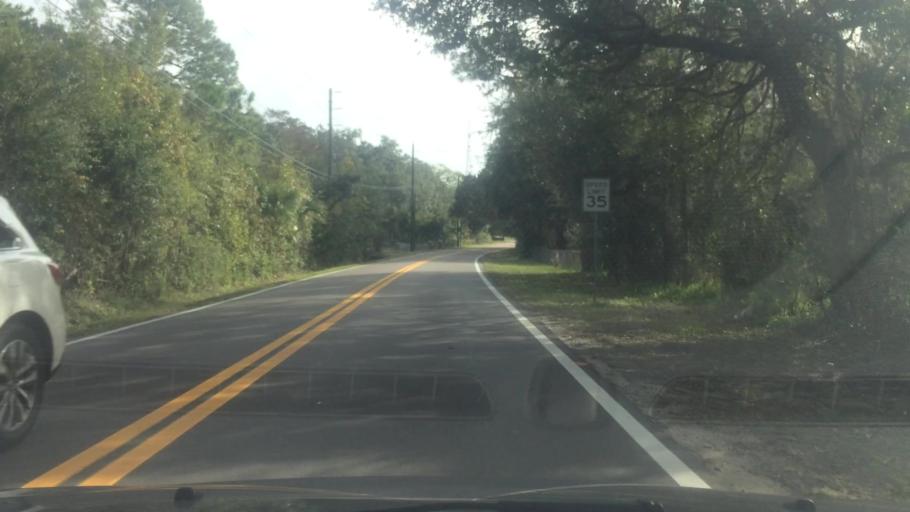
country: US
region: Florida
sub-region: Saint Johns County
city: Saint Augustine
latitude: 29.9220
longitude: -81.3609
